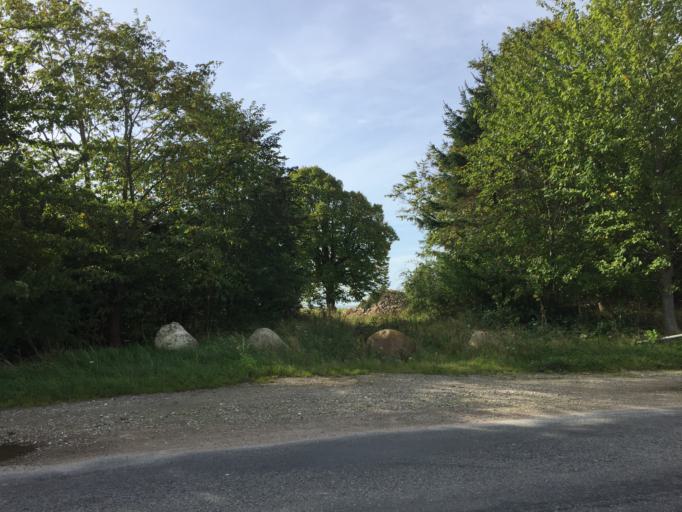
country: DK
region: Zealand
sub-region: Kalundborg Kommune
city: Kalundborg
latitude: 55.6574
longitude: 11.0524
